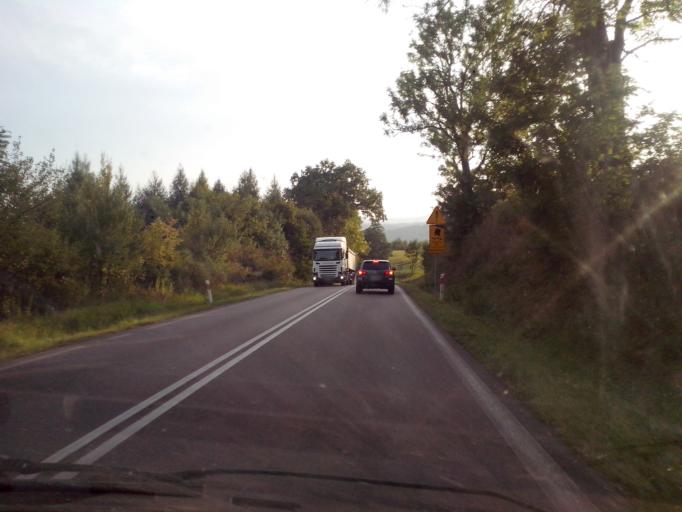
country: PL
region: Subcarpathian Voivodeship
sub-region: Powiat brzozowski
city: Domaradz
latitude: 49.8018
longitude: 21.9501
